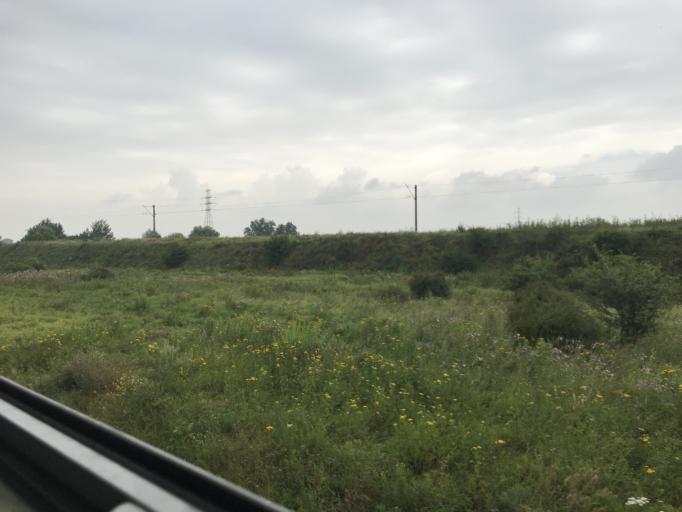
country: PL
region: Pomeranian Voivodeship
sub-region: Powiat tczewski
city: Tczew
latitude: 54.1068
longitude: 18.7812
